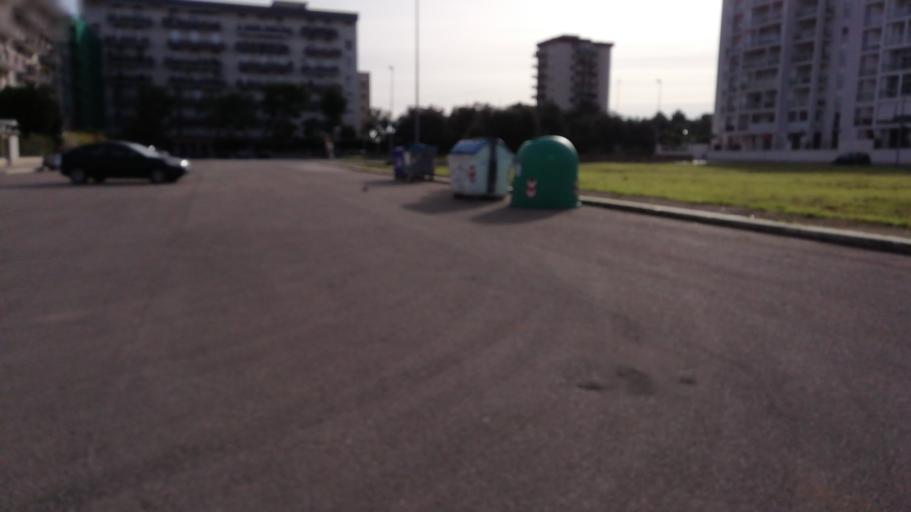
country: IT
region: Apulia
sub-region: Provincia di Bari
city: Triggiano
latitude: 41.1034
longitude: 16.9153
